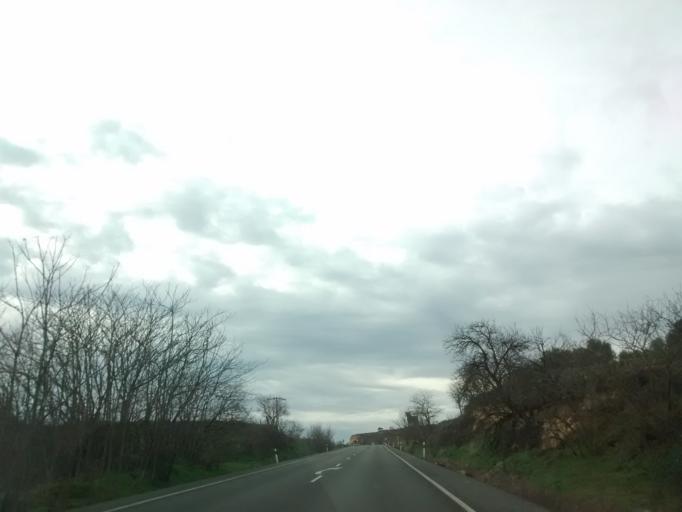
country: ES
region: La Rioja
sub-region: Provincia de La Rioja
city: Torremontalbo
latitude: 42.5099
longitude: -2.7160
